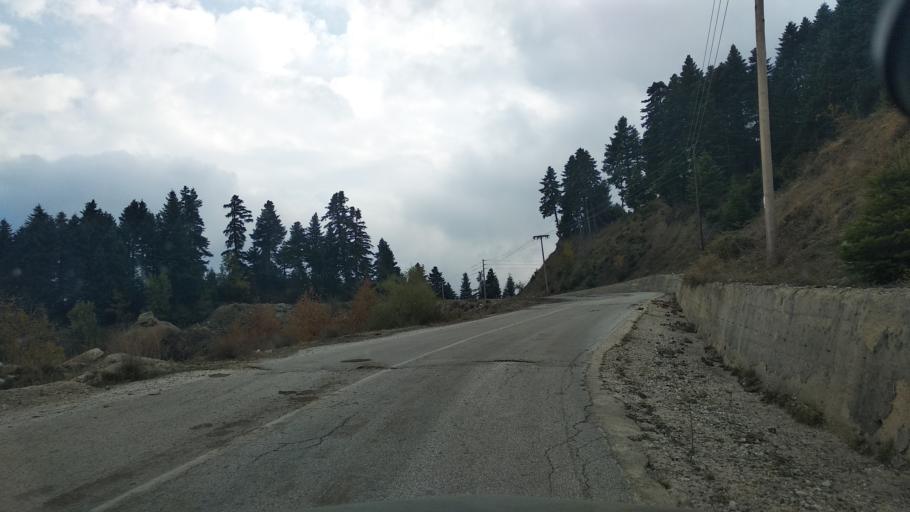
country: GR
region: Thessaly
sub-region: Trikala
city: Fiki
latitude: 39.5872
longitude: 21.4916
